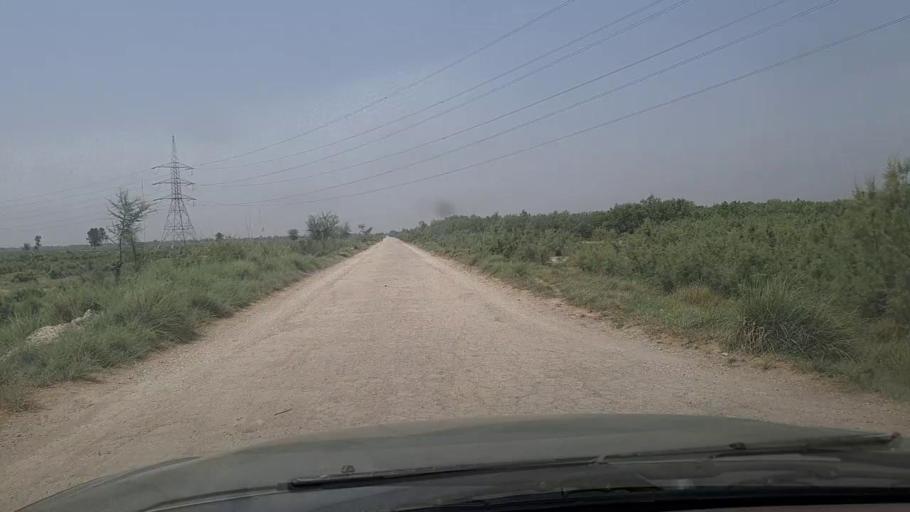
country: PK
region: Sindh
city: Adilpur
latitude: 27.9378
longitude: 69.2934
